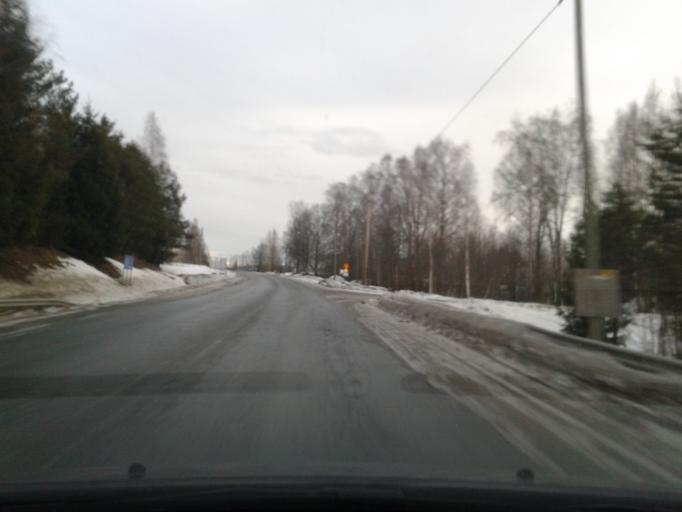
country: SE
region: Vaesternorrland
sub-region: Solleftea Kommun
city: Solleftea
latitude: 63.2417
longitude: 17.2074
